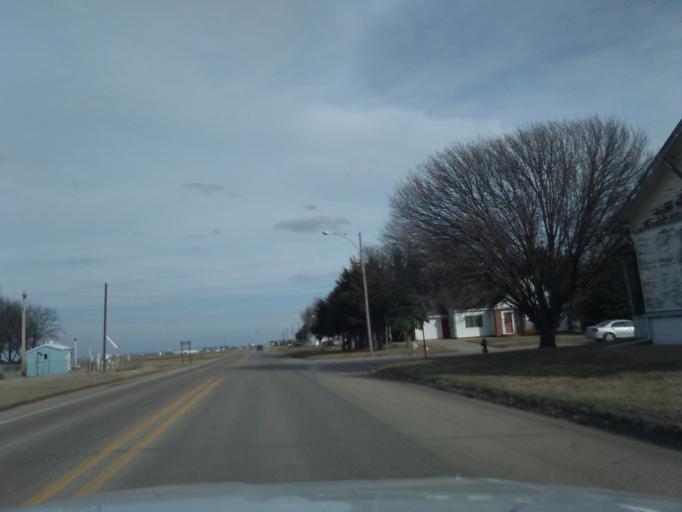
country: US
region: Nebraska
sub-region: Saline County
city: Wilber
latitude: 40.3060
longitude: -96.9882
